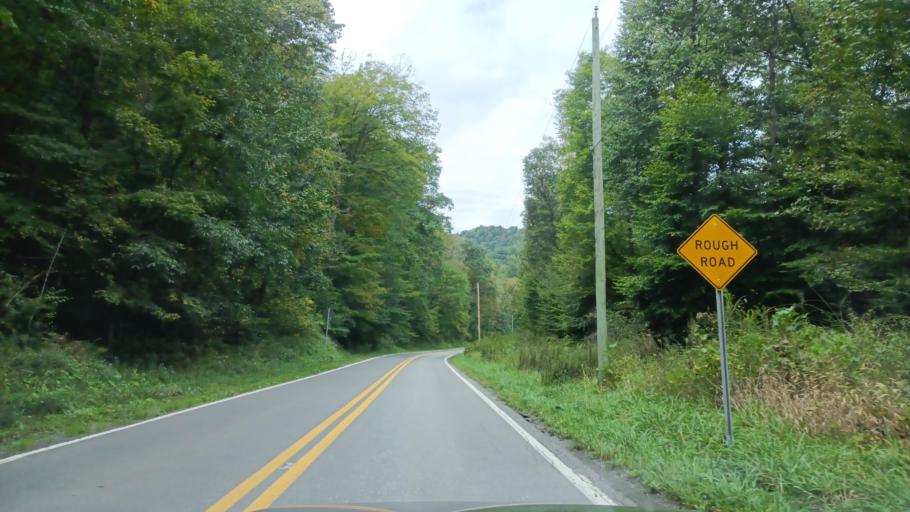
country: US
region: West Virginia
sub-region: Preston County
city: Kingwood
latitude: 39.3219
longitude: -79.7171
